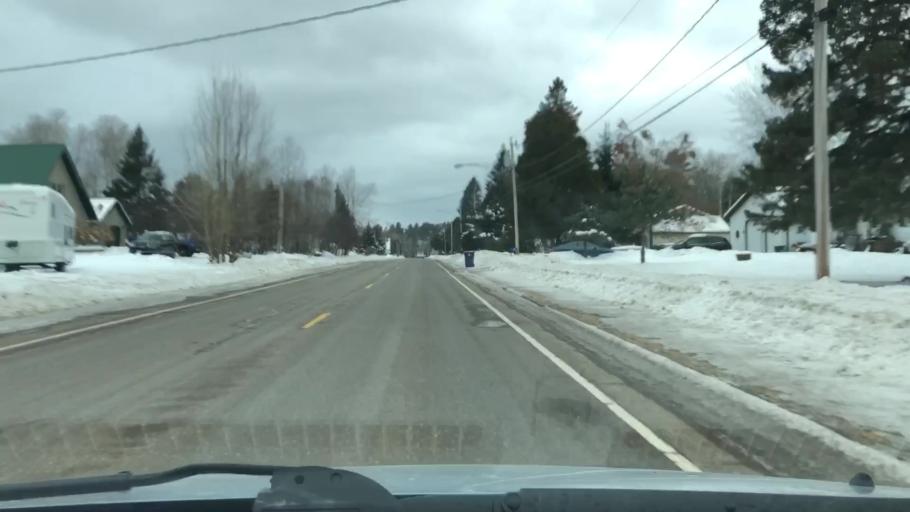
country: US
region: Minnesota
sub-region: Carlton County
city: Carlton
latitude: 46.6636
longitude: -92.3922
